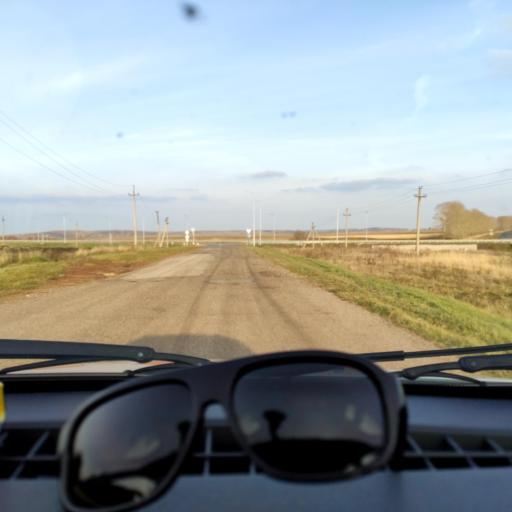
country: RU
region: Bashkortostan
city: Tolbazy
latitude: 53.9574
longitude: 55.9109
